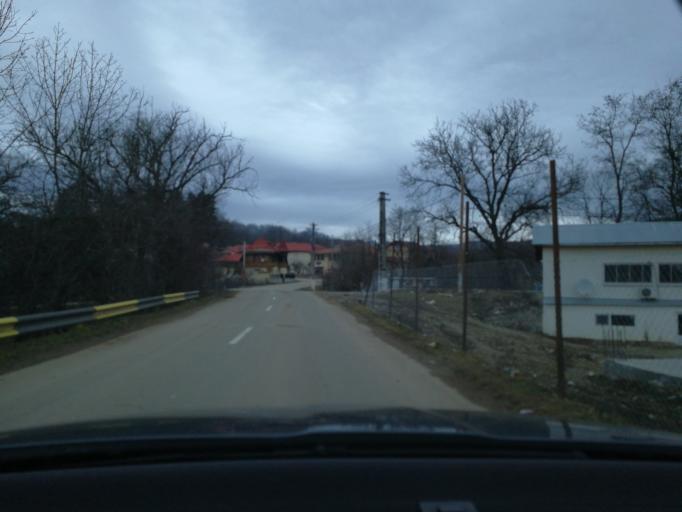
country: RO
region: Prahova
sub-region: Comuna Adunati
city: Ocina de Sus
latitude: 45.1823
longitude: 25.5996
